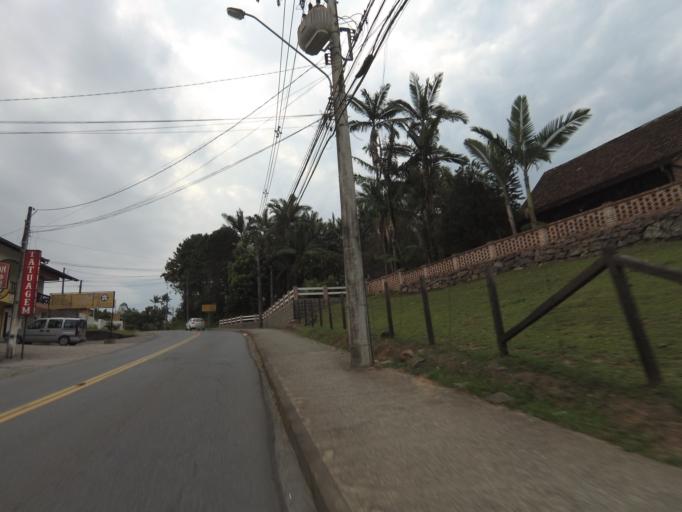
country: BR
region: Santa Catarina
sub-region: Blumenau
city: Blumenau
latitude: -26.8755
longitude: -49.0561
